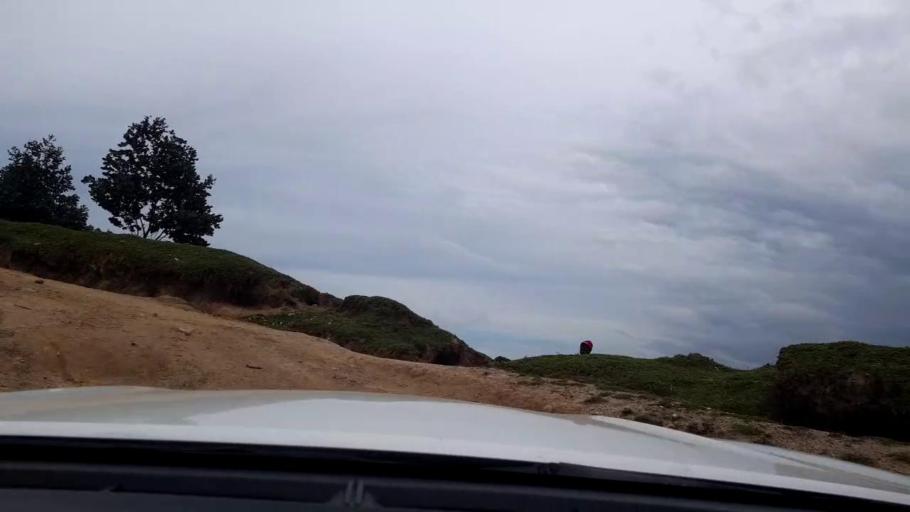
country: RW
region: Western Province
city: Kibuye
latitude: -1.8897
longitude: 29.4525
